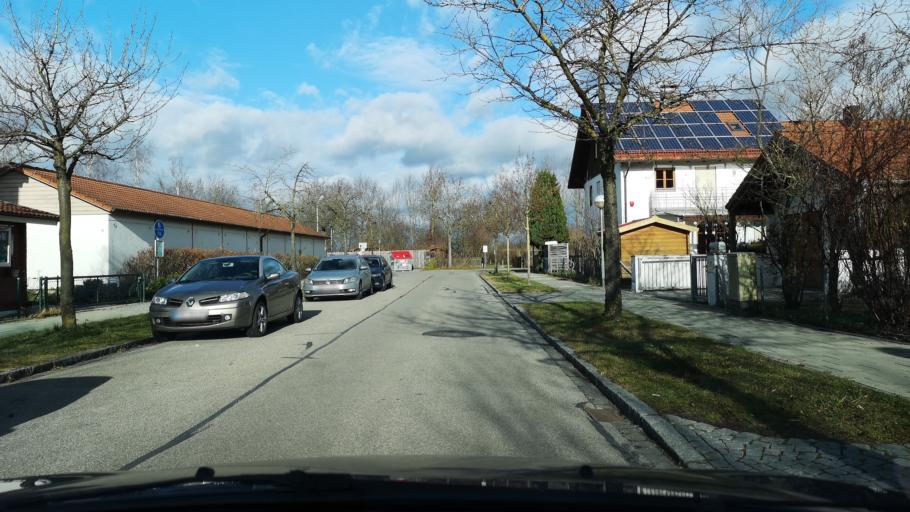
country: DE
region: Bavaria
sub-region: Upper Bavaria
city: Poing
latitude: 48.1796
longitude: 11.8053
